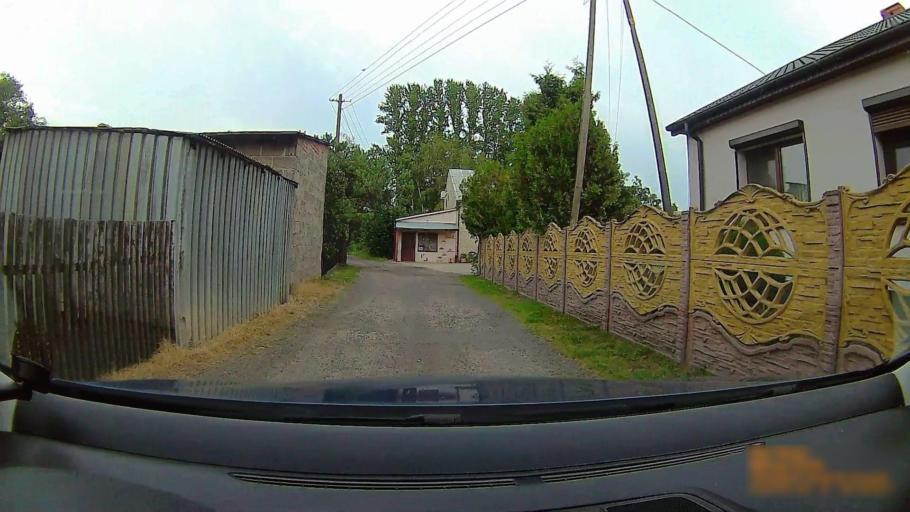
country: PL
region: Greater Poland Voivodeship
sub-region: Powiat koninski
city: Rychwal
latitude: 52.1182
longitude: 18.1695
